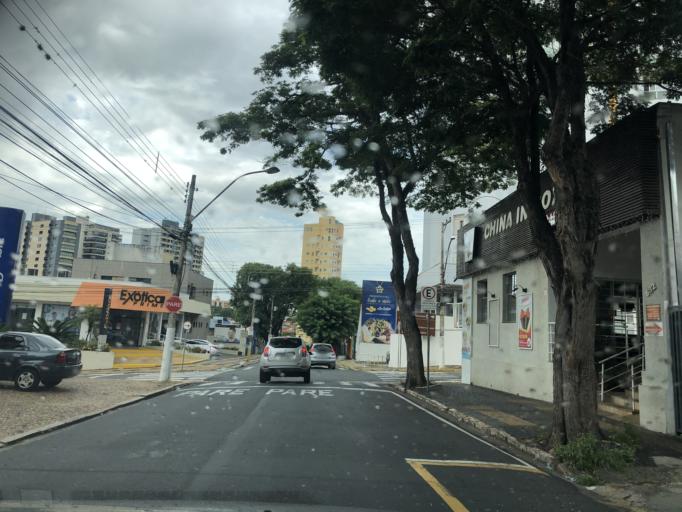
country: BR
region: Sao Paulo
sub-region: Americana
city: Americana
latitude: -22.7404
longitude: -47.3318
